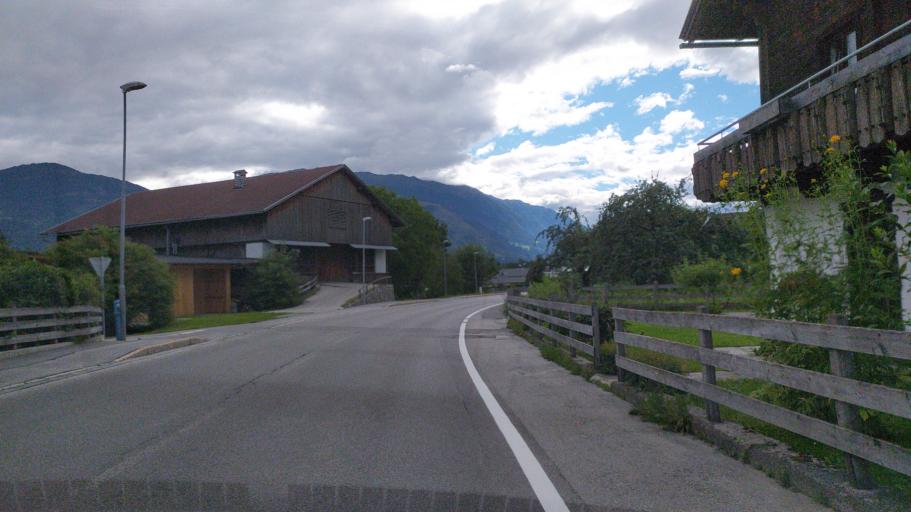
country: AT
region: Tyrol
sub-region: Politischer Bezirk Lienz
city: Tristach
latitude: 46.8194
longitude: 12.7907
